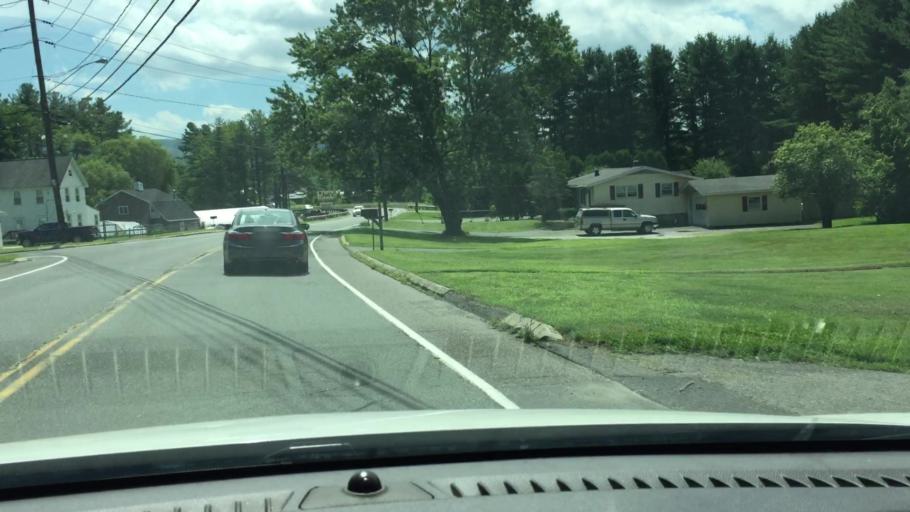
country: US
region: Massachusetts
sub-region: Berkshire County
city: Pittsfield
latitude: 42.4712
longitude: -73.2124
